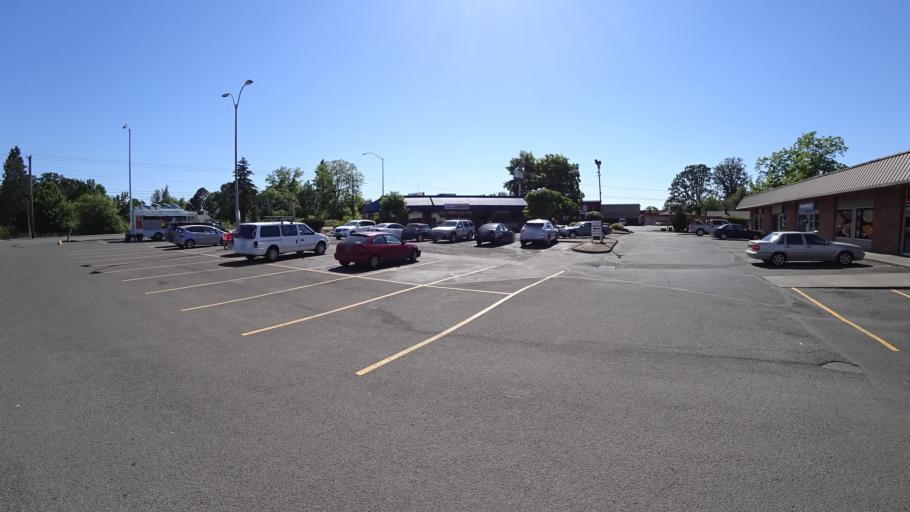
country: US
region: Oregon
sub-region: Washington County
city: Aloha
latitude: 45.4946
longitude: -122.8693
